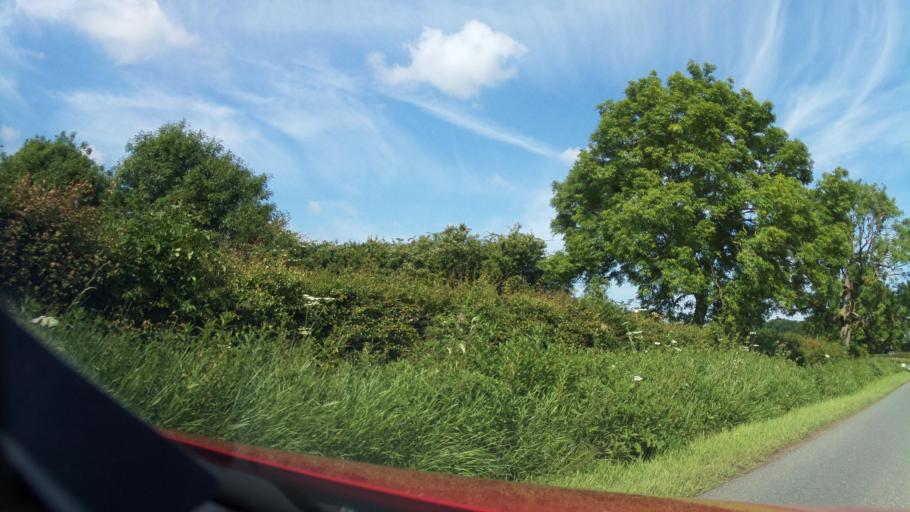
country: GB
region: England
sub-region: Lincolnshire
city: Skellingthorpe
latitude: 53.1585
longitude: -0.6351
